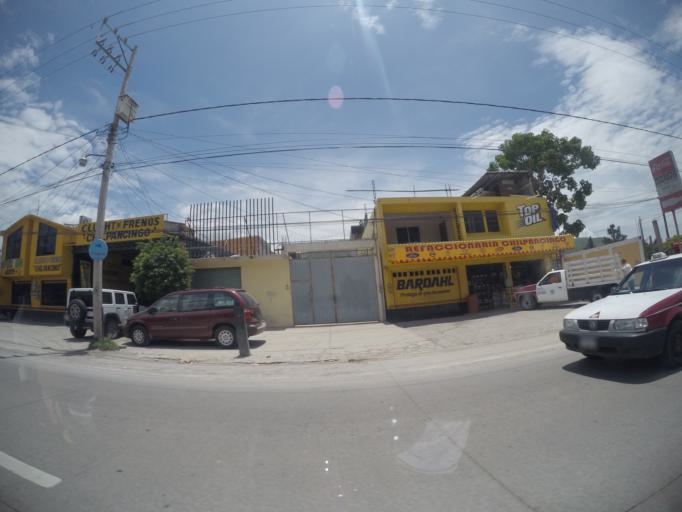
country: MX
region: Guerrero
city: Chilpancingo de los Bravos
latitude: 17.5714
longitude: -99.5124
